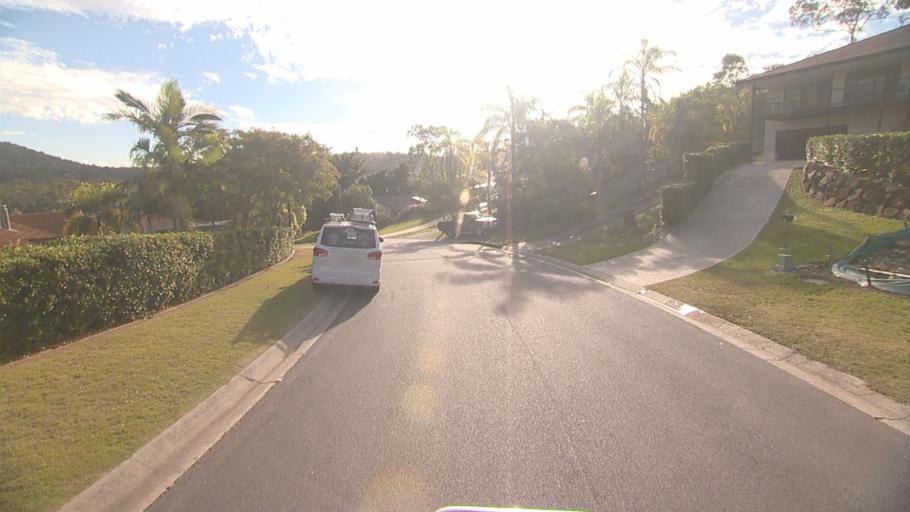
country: AU
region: Queensland
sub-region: Logan
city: Windaroo
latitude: -27.7342
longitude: 153.2014
